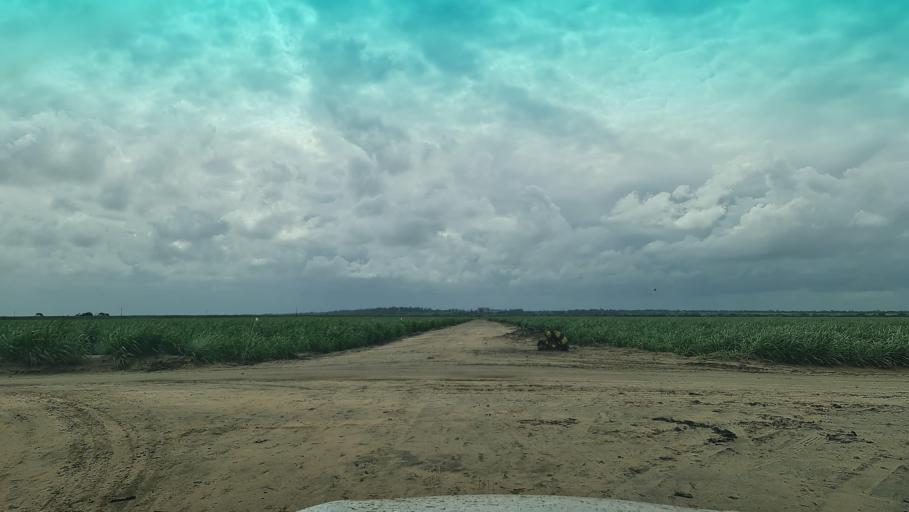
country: MZ
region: Maputo
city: Manhica
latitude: -25.4522
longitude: 32.8195
